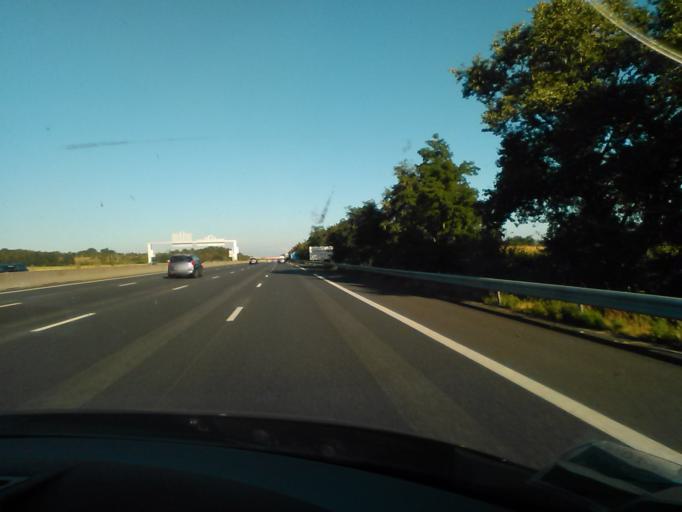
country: FR
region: Rhone-Alpes
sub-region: Departement de l'Isere
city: Grenay
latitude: 45.6643
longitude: 5.0617
